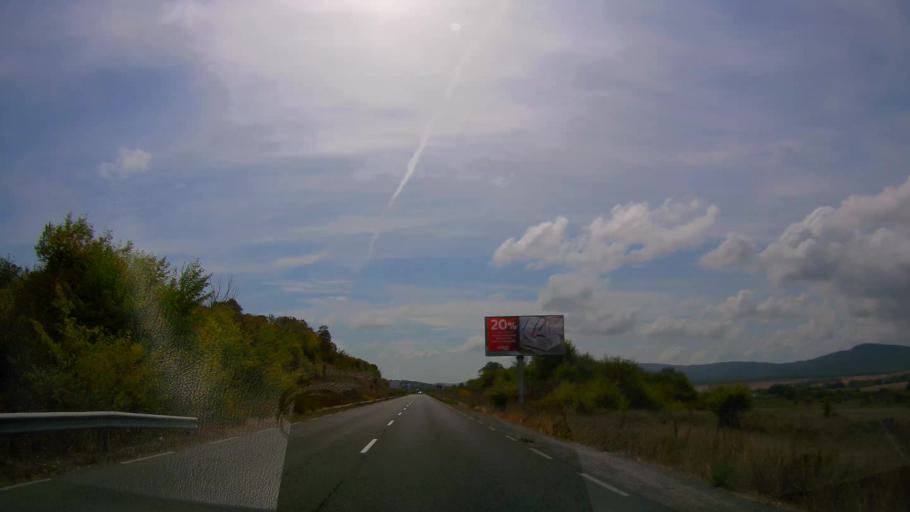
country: BG
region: Burgas
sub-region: Obshtina Sozopol
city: Sozopol
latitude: 42.3896
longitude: 27.6778
